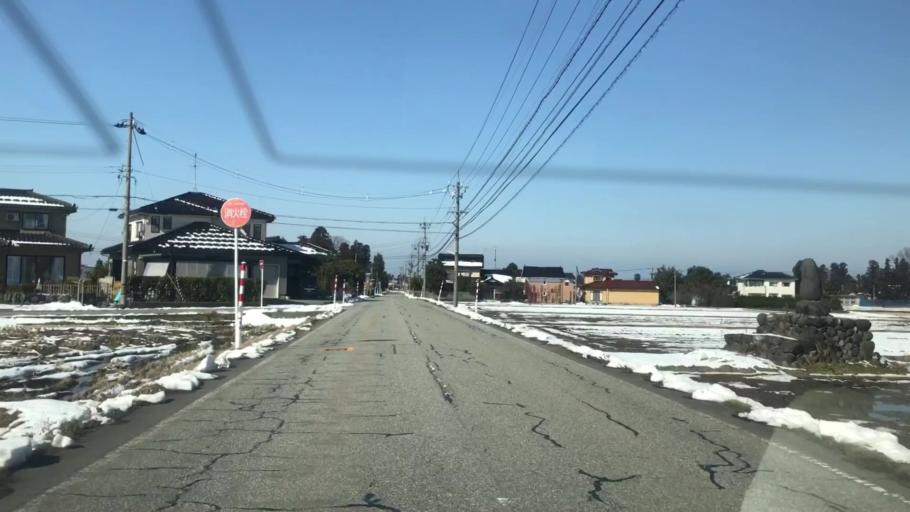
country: JP
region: Toyama
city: Toyama-shi
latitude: 36.6201
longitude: 137.2846
